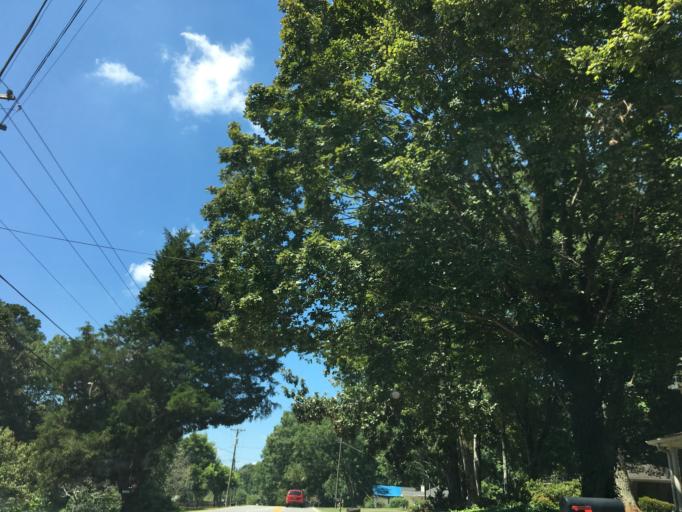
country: US
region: Georgia
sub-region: Fulton County
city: Milton
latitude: 34.1198
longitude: -84.3331
